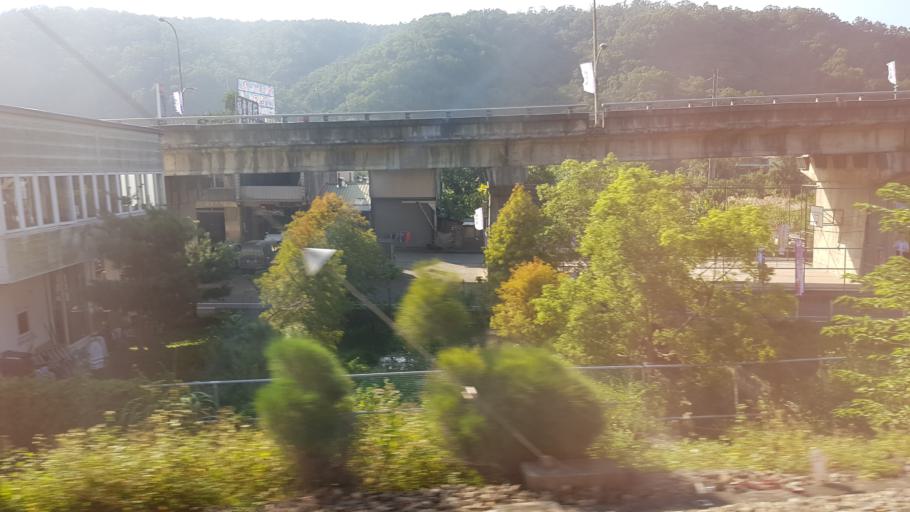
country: TW
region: Taiwan
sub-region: Miaoli
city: Miaoli
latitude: 24.4234
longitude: 120.7743
